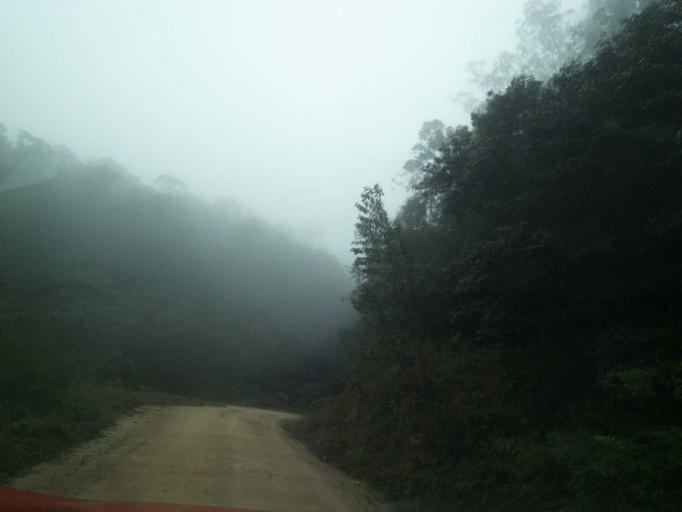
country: BR
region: Santa Catarina
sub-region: Anitapolis
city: Anitapolis
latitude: -27.9263
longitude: -49.1789
